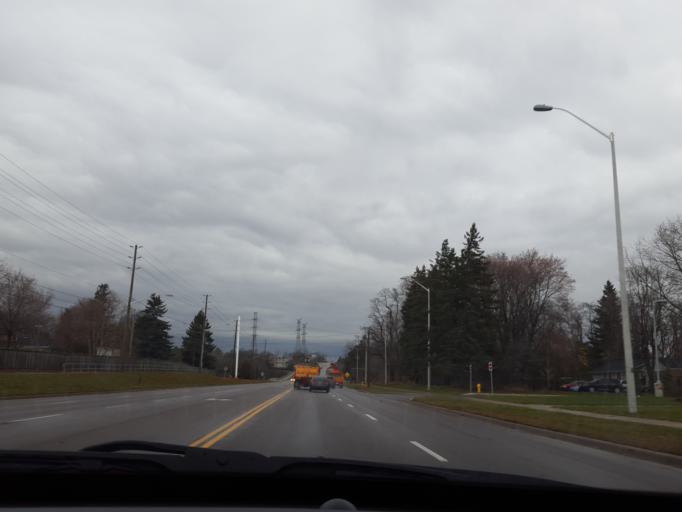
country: CA
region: Ontario
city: Ajax
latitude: 43.8599
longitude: -79.0797
